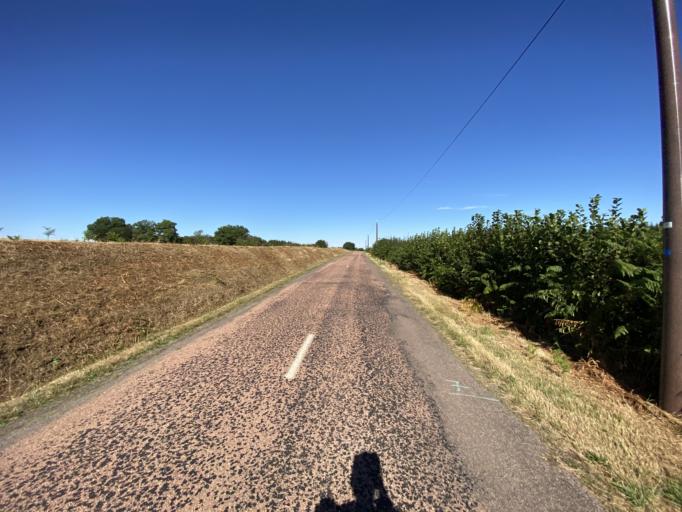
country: FR
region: Bourgogne
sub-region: Departement de la Cote-d'Or
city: Saulieu
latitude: 47.2726
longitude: 4.1649
